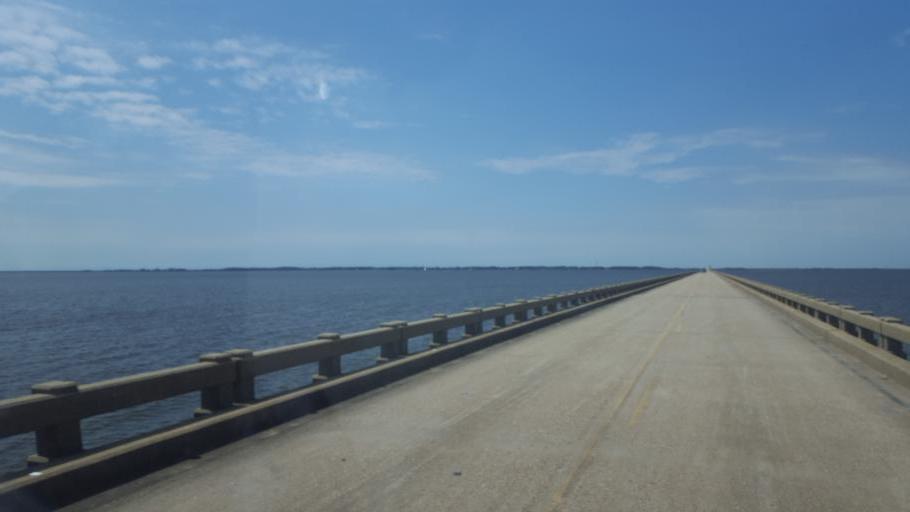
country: US
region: North Carolina
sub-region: Dare County
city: Manteo
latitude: 35.9263
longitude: -75.7264
